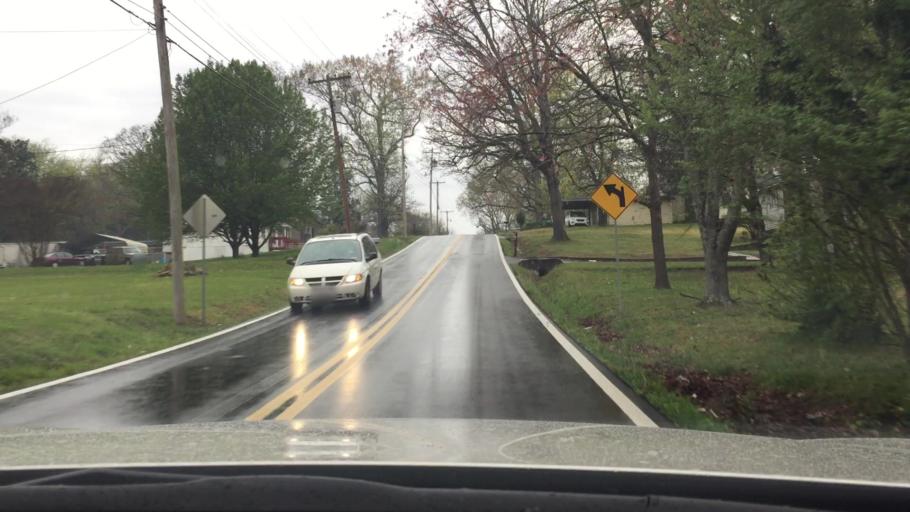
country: US
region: Georgia
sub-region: Catoosa County
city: Lakeview
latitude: 34.9806
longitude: -85.2486
